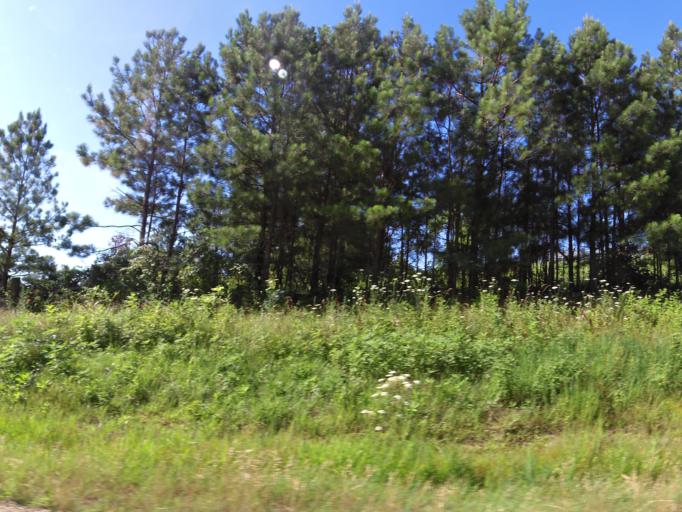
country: US
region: Arkansas
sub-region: Clay County
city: Piggott
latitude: 36.4337
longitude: -90.3301
